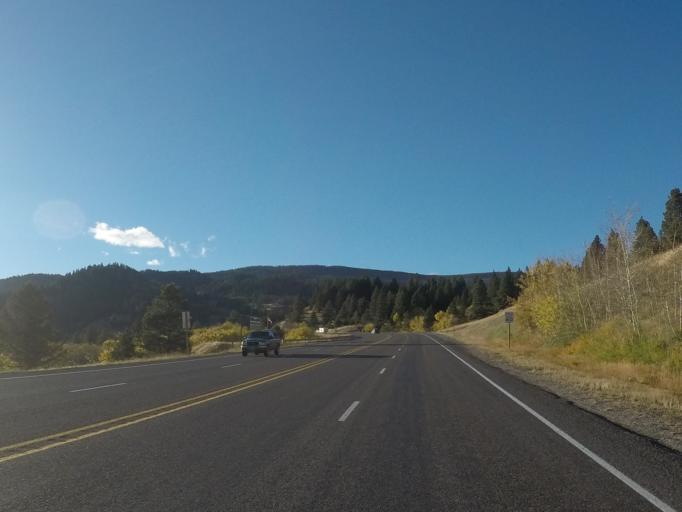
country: US
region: Montana
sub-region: Lewis and Clark County
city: Helena West Side
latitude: 46.5781
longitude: -112.2526
